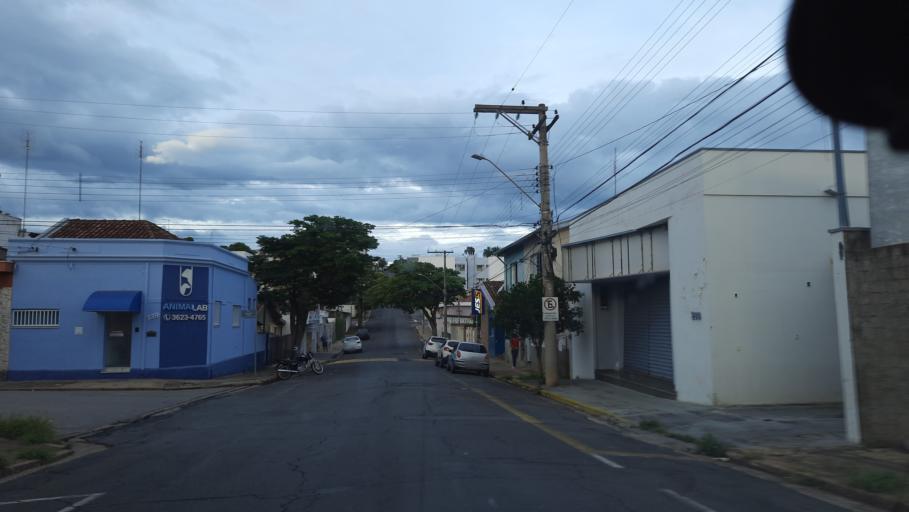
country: BR
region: Sao Paulo
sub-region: Sao Joao Da Boa Vista
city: Sao Joao da Boa Vista
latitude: -21.9675
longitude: -46.7945
